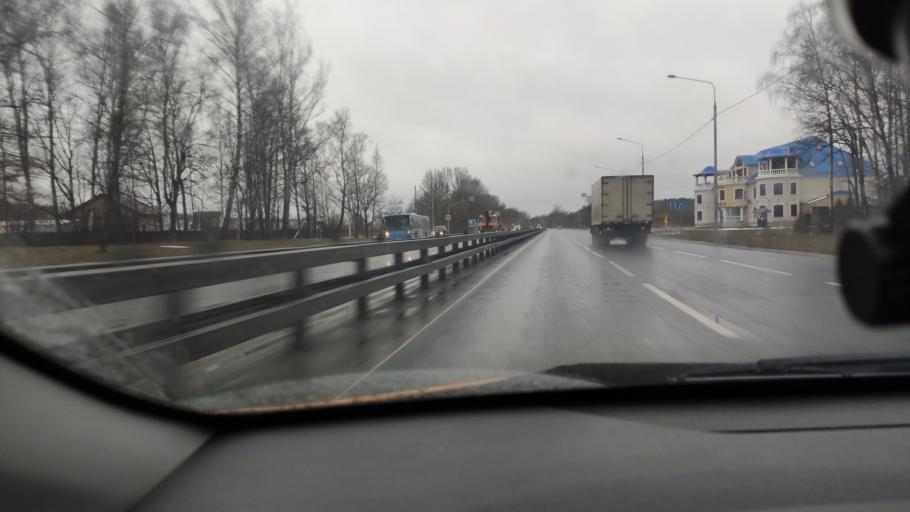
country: RU
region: Moskovskaya
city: Troitsk
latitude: 55.3119
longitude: 37.2338
